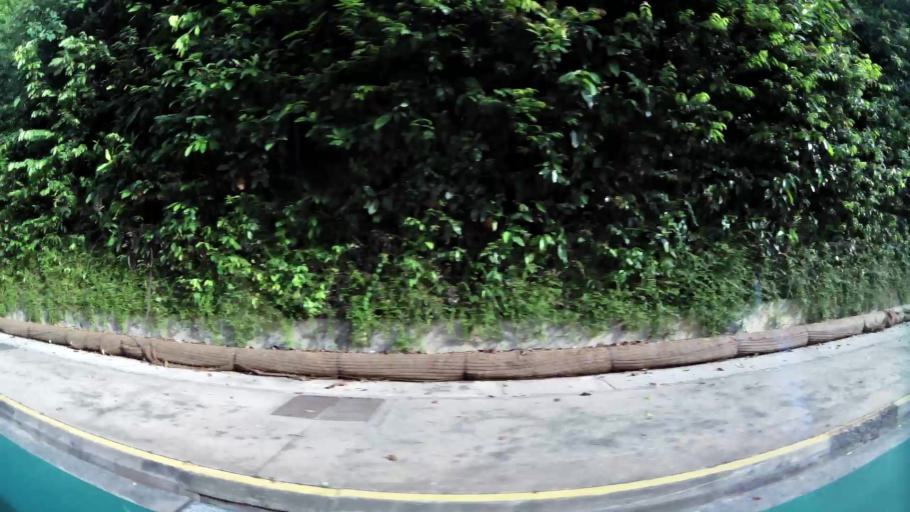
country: SG
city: Singapore
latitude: 1.2479
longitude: 103.8324
